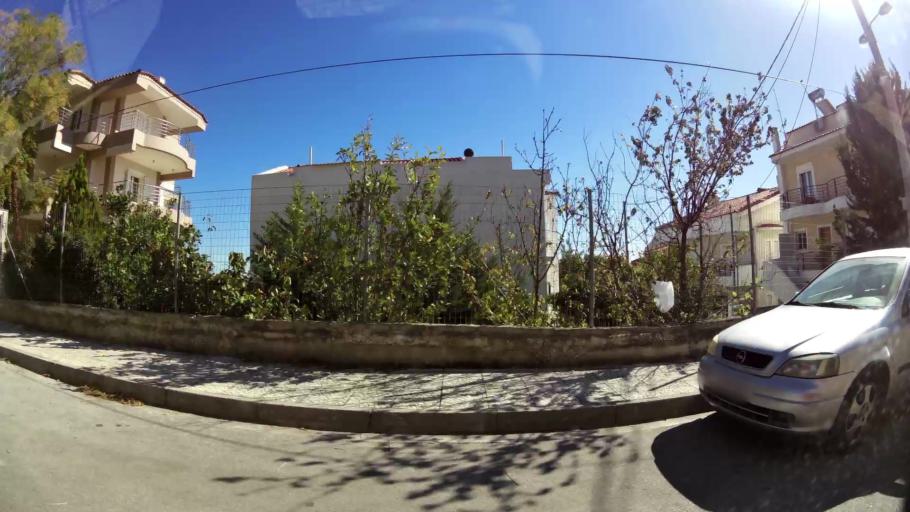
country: GR
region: Attica
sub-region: Nomarchia Anatolikis Attikis
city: Leondarion
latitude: 38.0019
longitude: 23.8501
